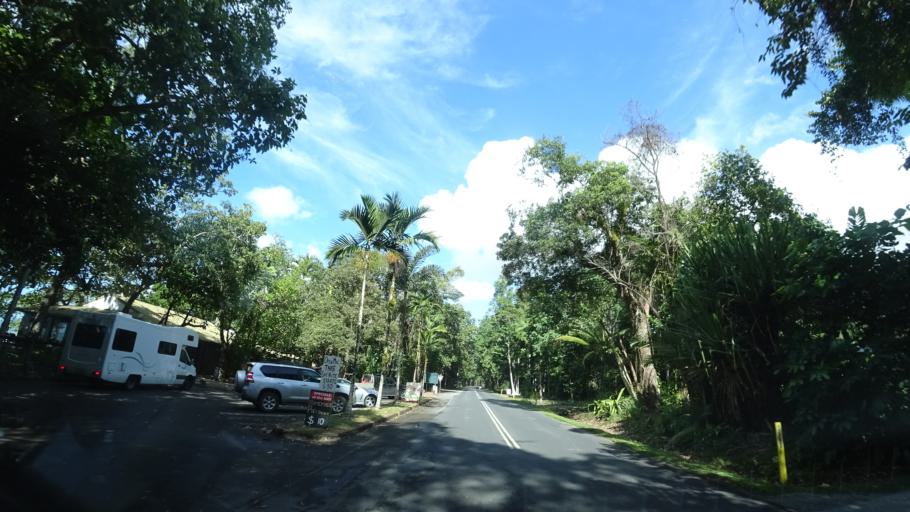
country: AU
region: Queensland
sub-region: Cairns
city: Port Douglas
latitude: -16.1720
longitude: 145.4418
